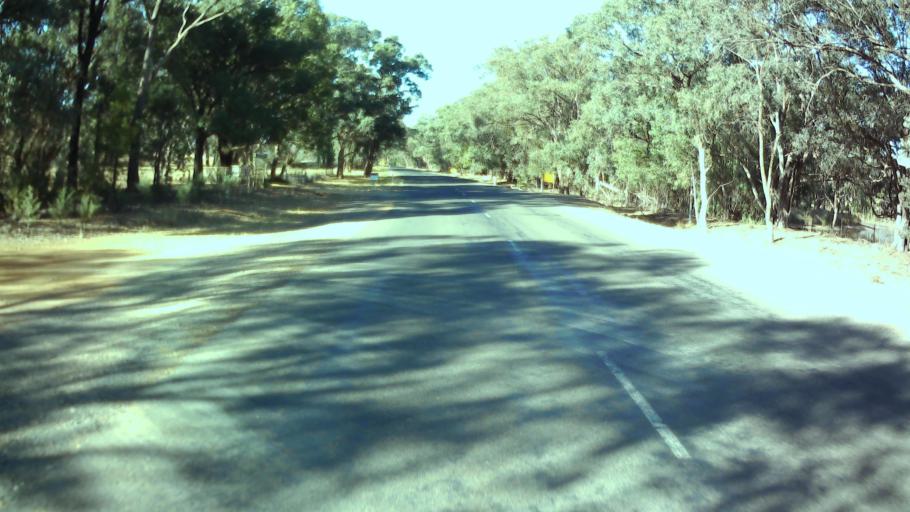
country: AU
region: New South Wales
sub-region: Weddin
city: Grenfell
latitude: -33.9903
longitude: 148.1374
